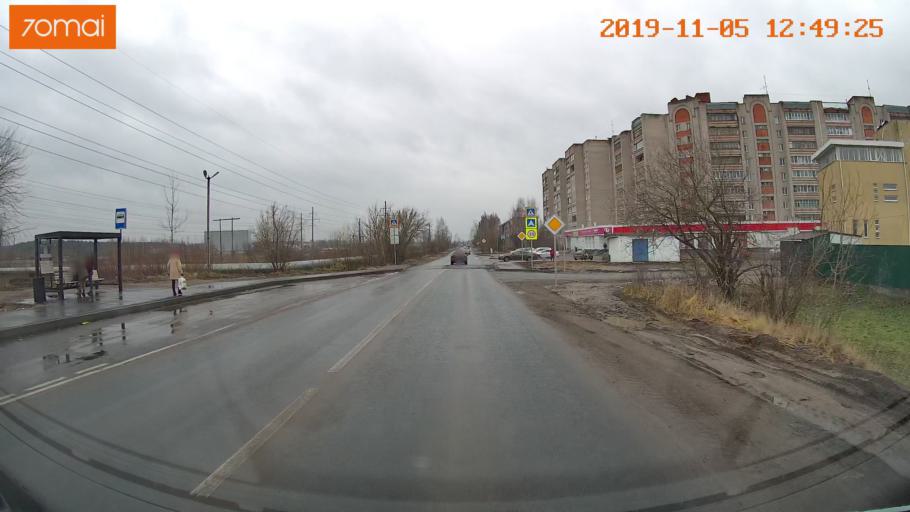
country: RU
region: Ivanovo
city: Kokhma
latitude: 56.9548
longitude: 41.1040
